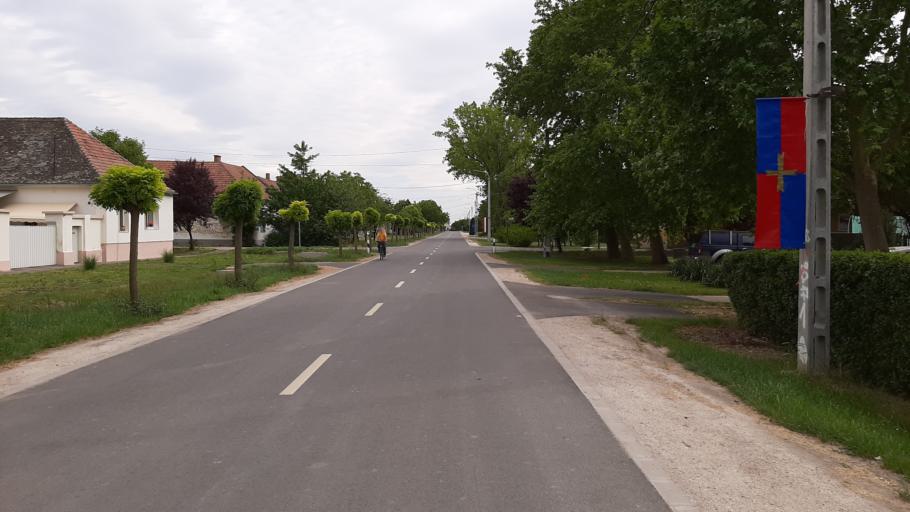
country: RO
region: Timis
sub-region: Comuna Beba Veche
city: Beba Veche
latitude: 46.1481
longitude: 20.2757
